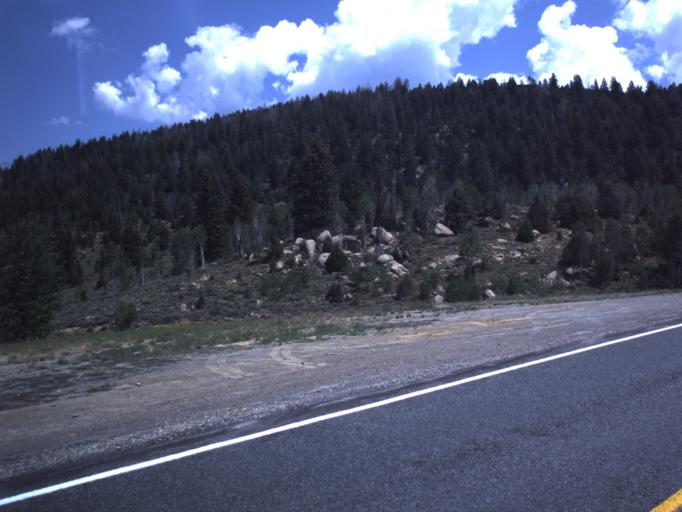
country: US
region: Utah
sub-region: Carbon County
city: Helper
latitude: 39.8644
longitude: -111.1200
